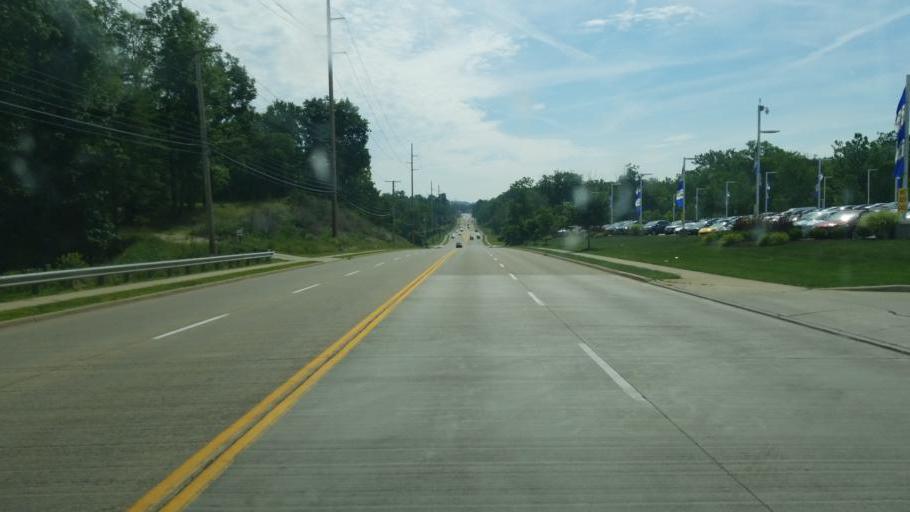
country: US
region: Ohio
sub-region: Cuyahoga County
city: Strongsville
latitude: 41.3132
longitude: -81.8028
